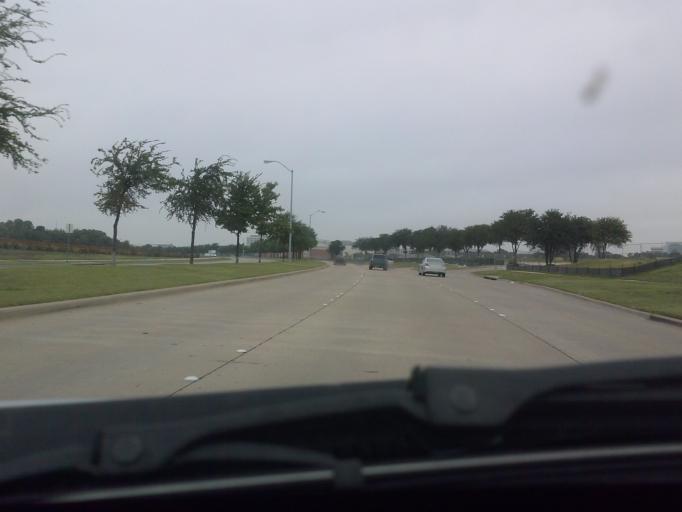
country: US
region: Texas
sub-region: Denton County
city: The Colony
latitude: 33.0629
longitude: -96.8123
